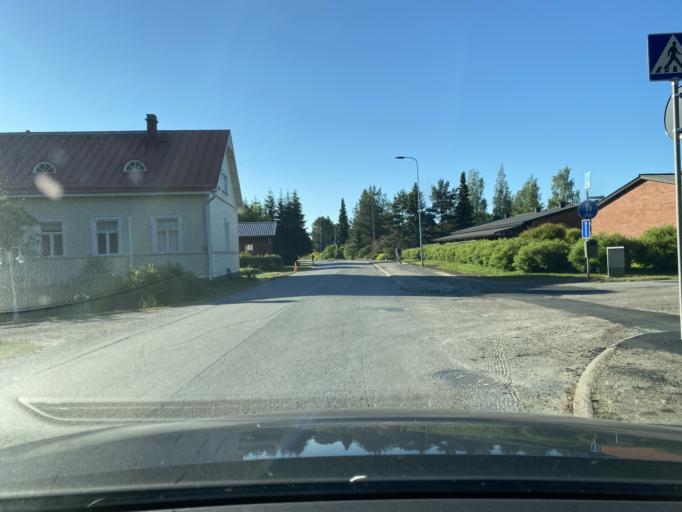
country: FI
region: Satakunta
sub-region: Pori
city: Huittinen
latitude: 61.1706
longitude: 22.6989
